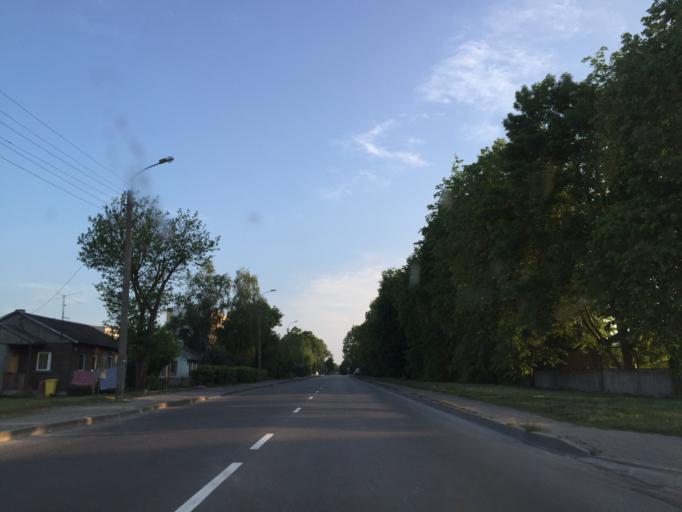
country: LT
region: Siauliu apskritis
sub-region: Siauliai
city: Siauliai
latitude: 55.9527
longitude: 23.3273
